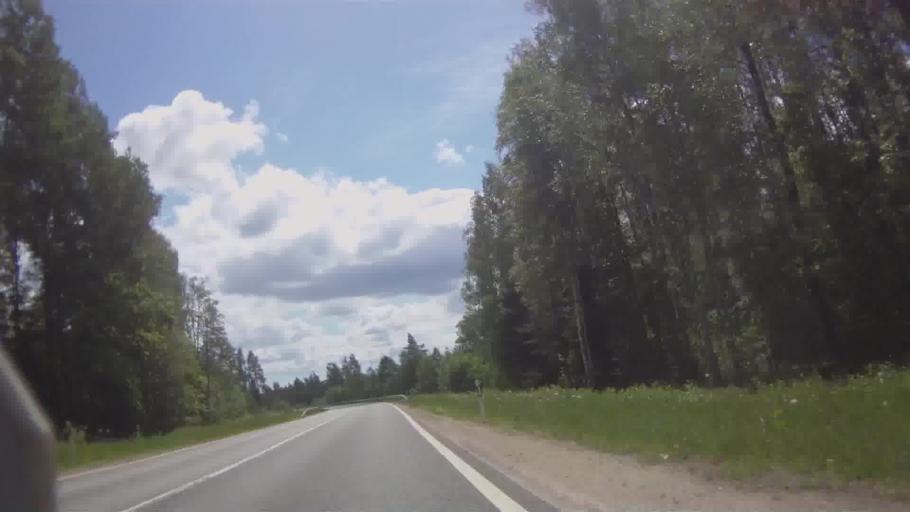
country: LV
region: Livani
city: Livani
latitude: 56.5326
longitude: 26.1402
